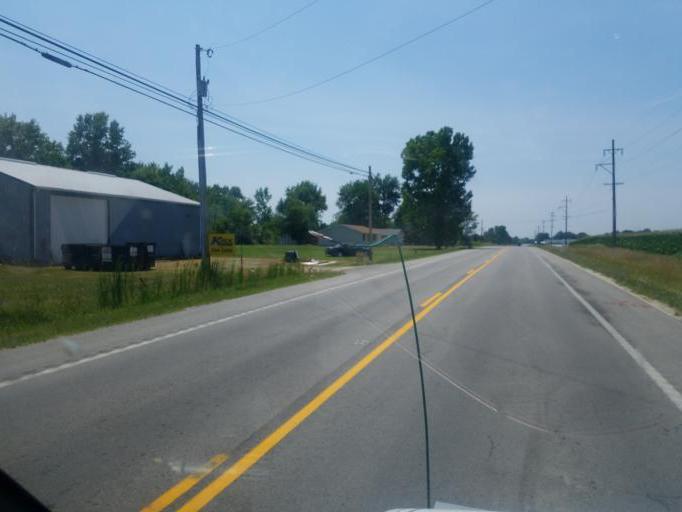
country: US
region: Ohio
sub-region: Auglaize County
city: Saint Marys
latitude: 40.5510
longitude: -84.4558
